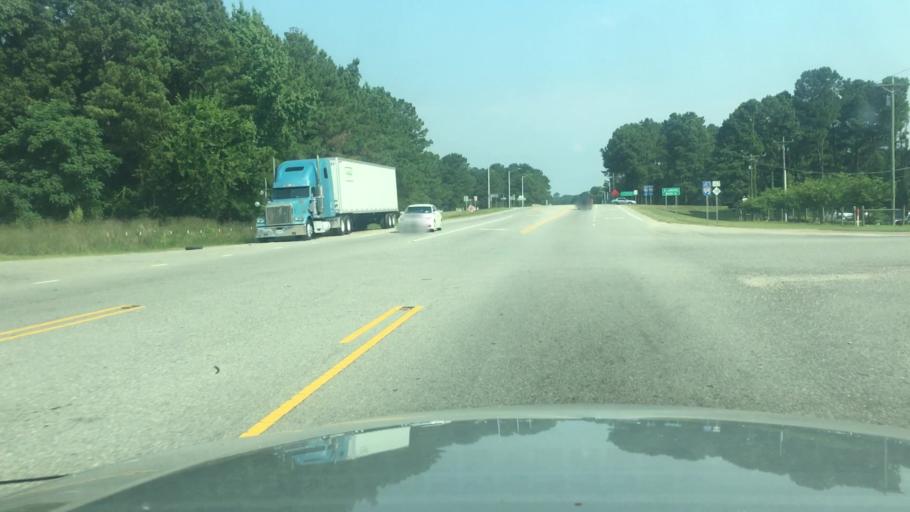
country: US
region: North Carolina
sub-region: Cumberland County
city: Hope Mills
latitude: 34.9358
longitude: -78.9211
